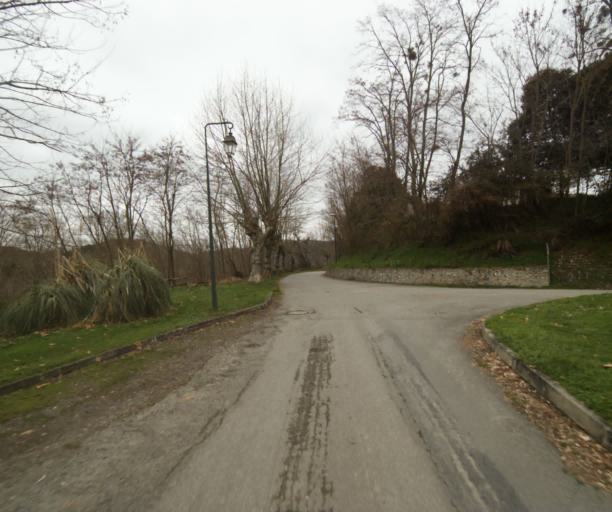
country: FR
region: Midi-Pyrenees
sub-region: Departement de l'Ariege
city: Pamiers
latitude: 43.1650
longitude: 1.5977
